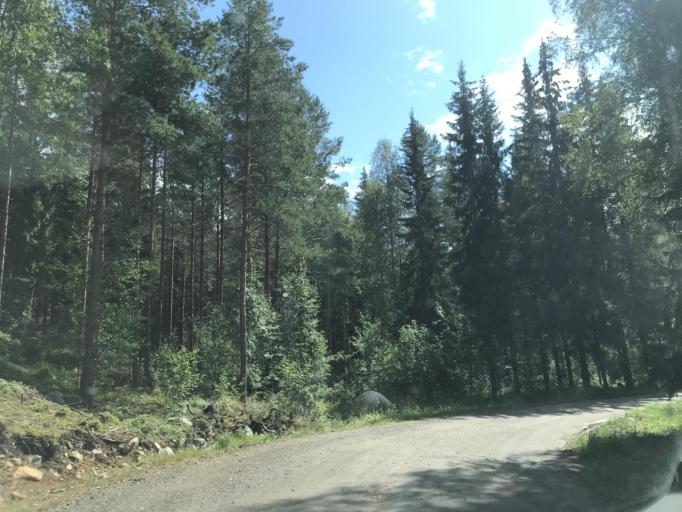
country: FI
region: Haeme
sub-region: Forssa
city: Tammela
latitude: 60.6281
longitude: 23.7578
